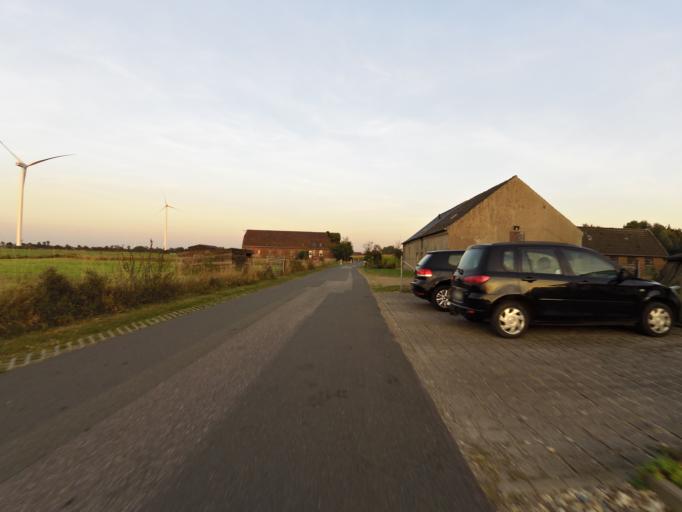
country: DE
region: North Rhine-Westphalia
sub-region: Regierungsbezirk Dusseldorf
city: Emmerich
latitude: 51.8584
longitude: 6.2497
